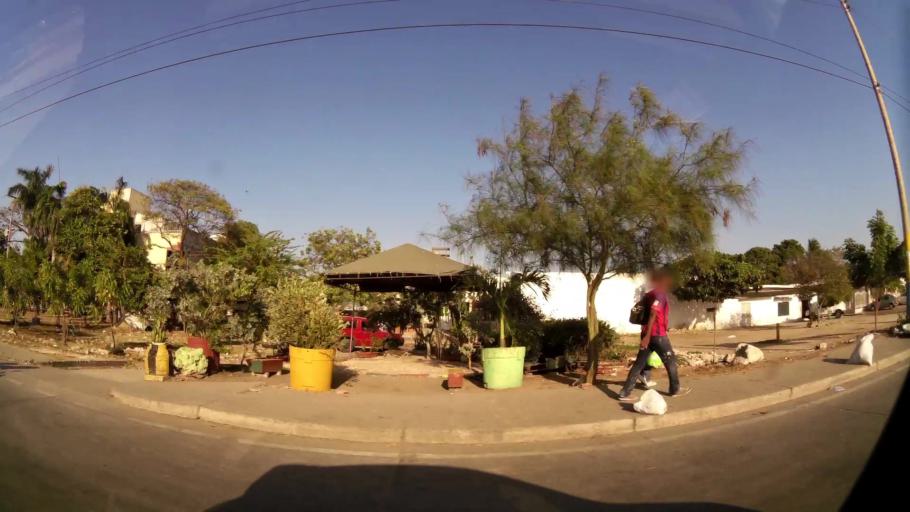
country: CO
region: Bolivar
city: Cartagena
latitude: 10.4094
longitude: -75.5234
